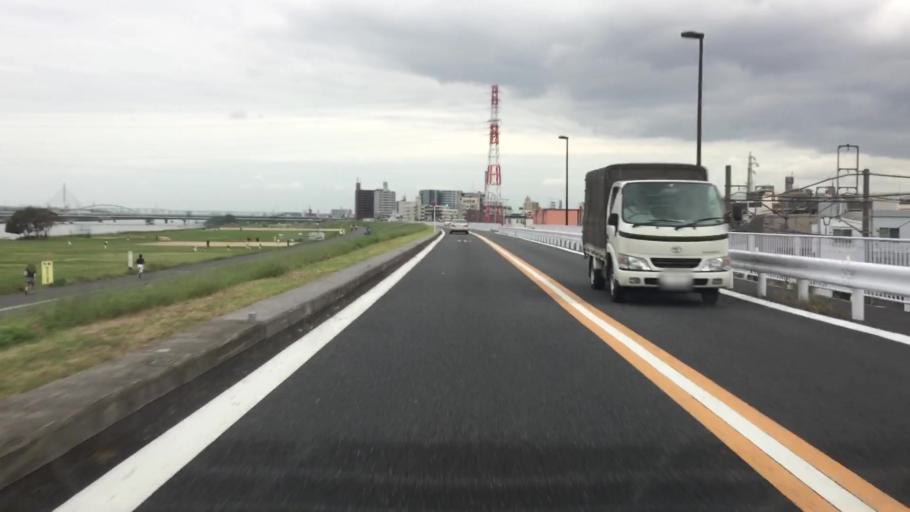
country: JP
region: Saitama
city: Soka
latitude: 35.7382
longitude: 139.8207
